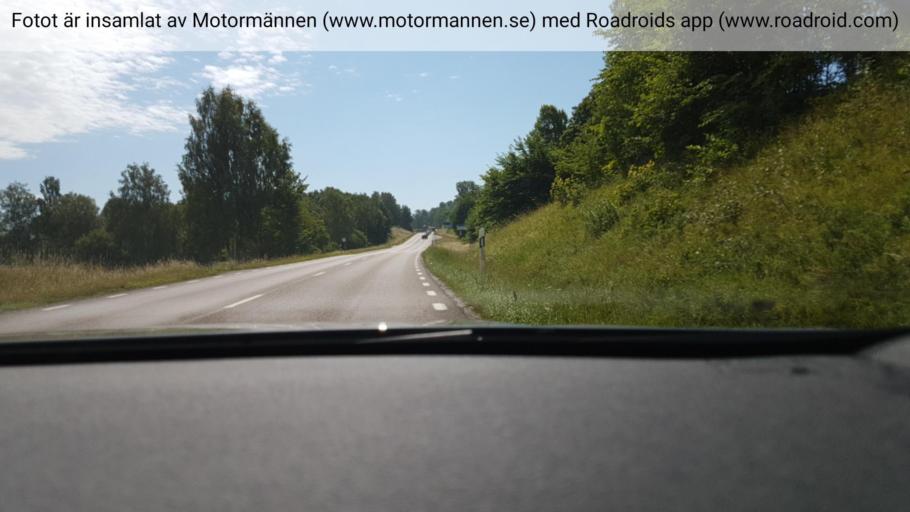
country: SE
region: Vaestra Goetaland
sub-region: Falkopings Kommun
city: Akarp
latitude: 58.1317
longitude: 13.6542
